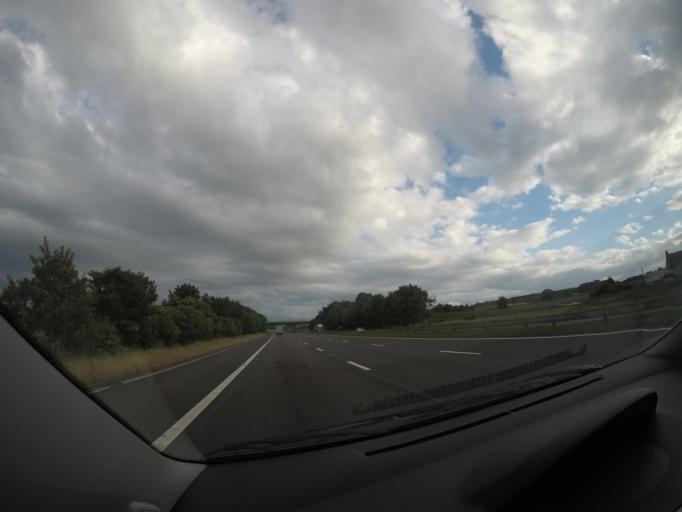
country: GB
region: England
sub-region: Cumbria
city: Penrith
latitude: 54.7245
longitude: -2.8007
